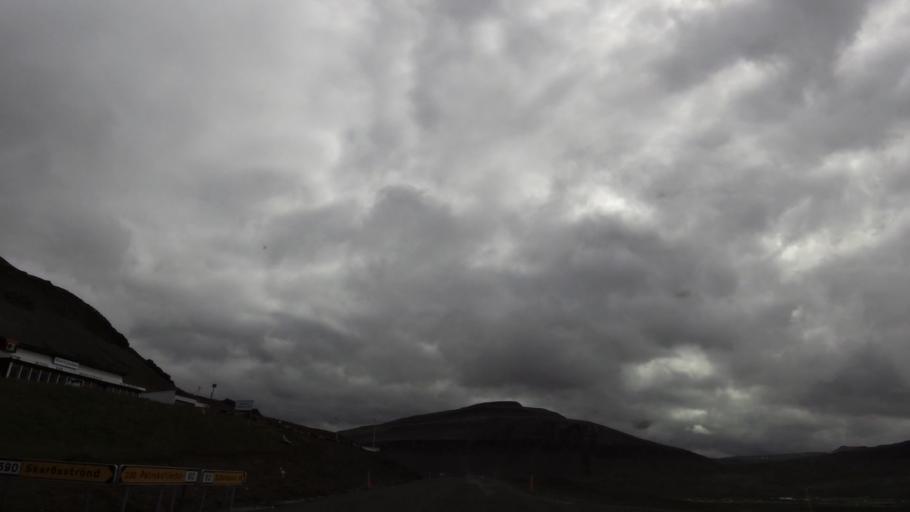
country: IS
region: West
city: Borgarnes
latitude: 65.3823
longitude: -21.8769
